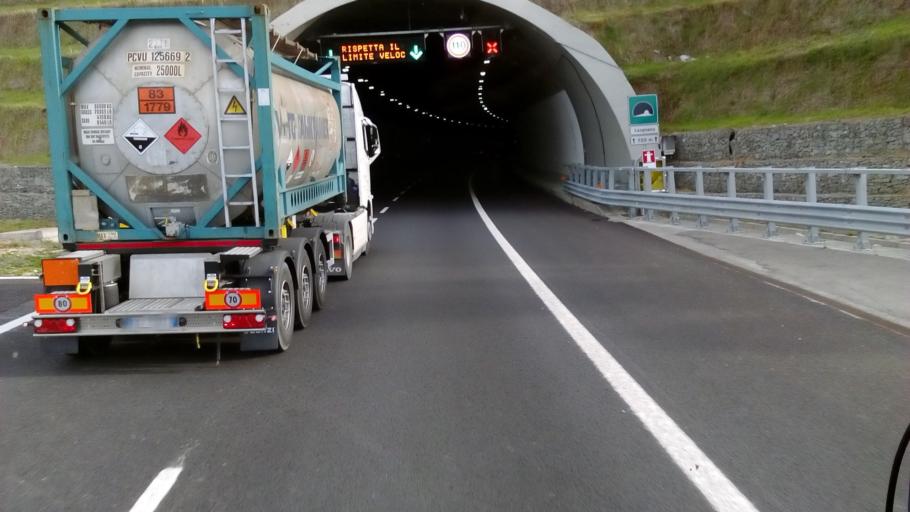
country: IT
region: Tuscany
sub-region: Province of Florence
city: Barberino di Mugello
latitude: 44.0384
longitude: 11.2281
